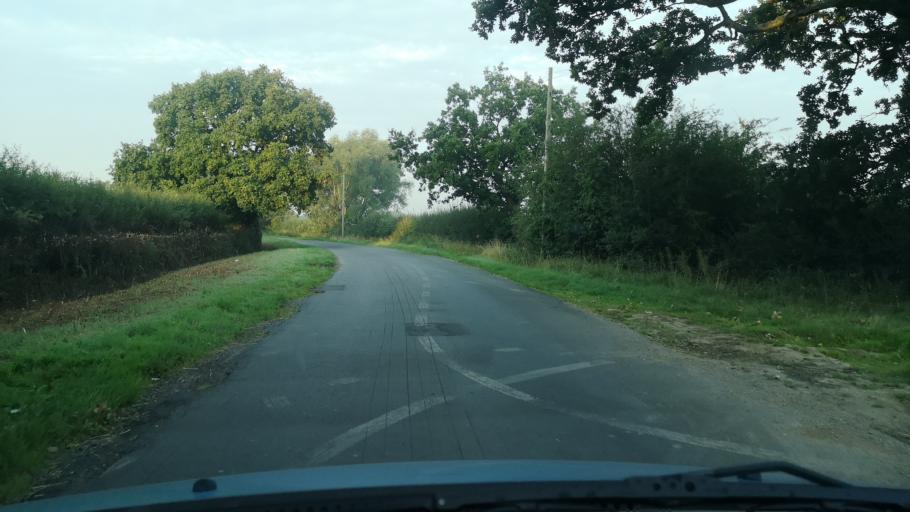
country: GB
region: England
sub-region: Doncaster
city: Stainforth
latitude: 53.6132
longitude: -1.0645
